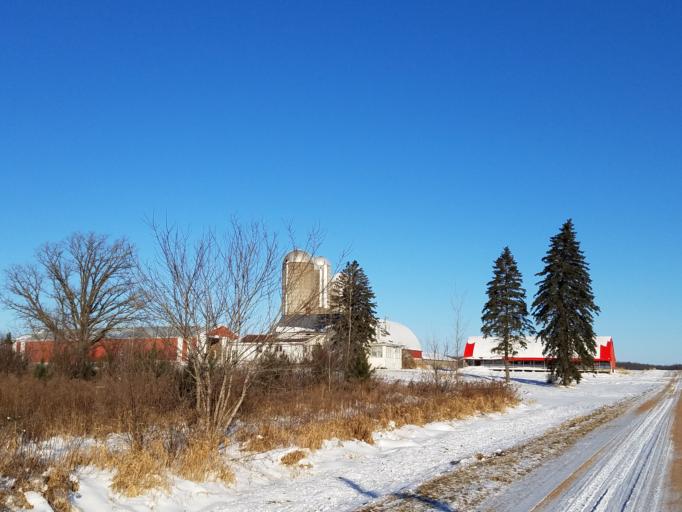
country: US
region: Wisconsin
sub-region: Clark County
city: Loyal
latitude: 44.6319
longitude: -90.4071
